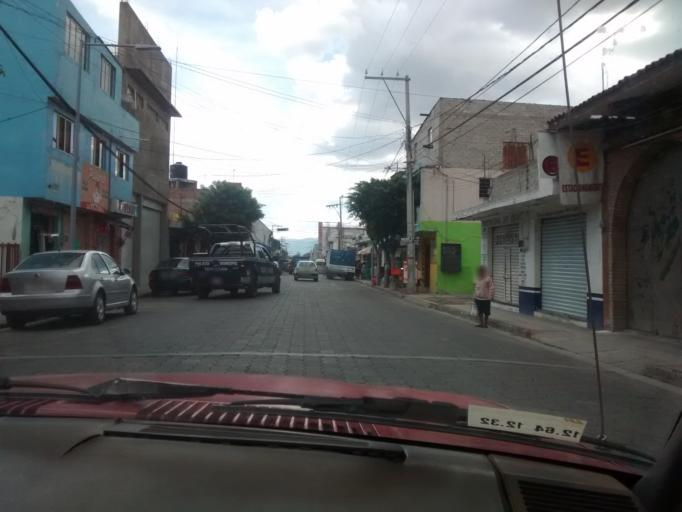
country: MX
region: Puebla
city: Tehuacan
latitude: 18.4591
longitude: -97.3851
